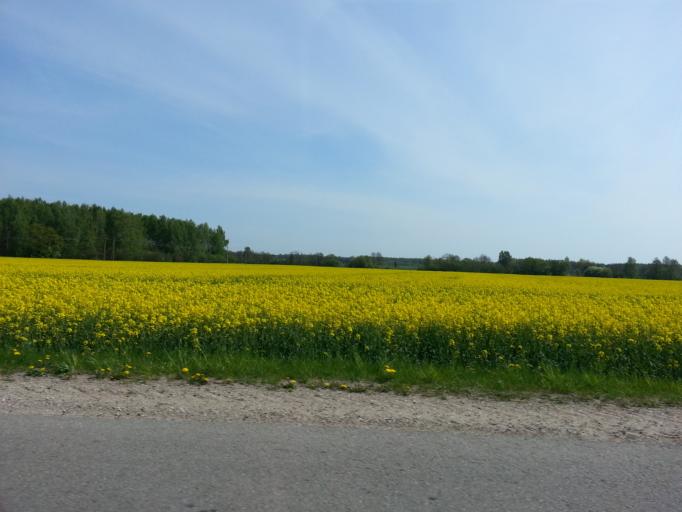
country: LT
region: Panevezys
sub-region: Panevezys City
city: Panevezys
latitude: 55.8399
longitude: 24.2531
